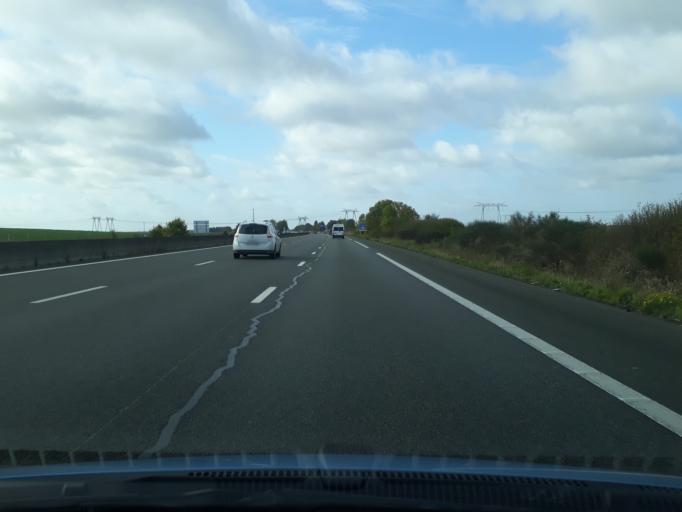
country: FR
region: Centre
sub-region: Departement du Loiret
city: Tavers
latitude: 47.7658
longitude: 1.5644
